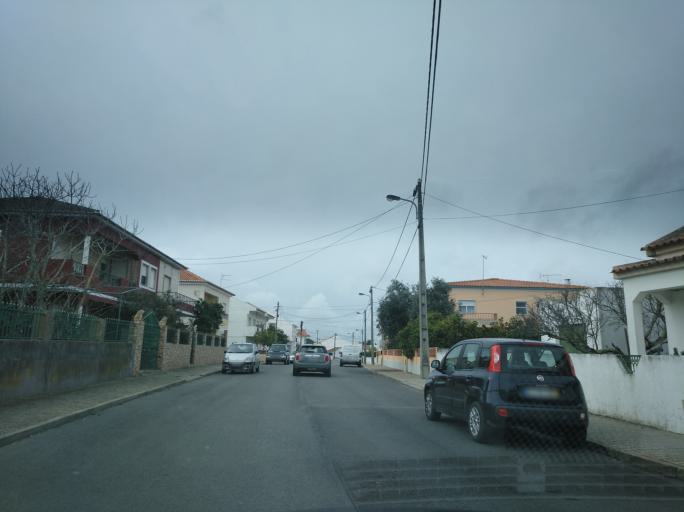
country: PT
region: Setubal
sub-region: Grandola
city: Grandola
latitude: 38.1782
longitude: -8.5693
